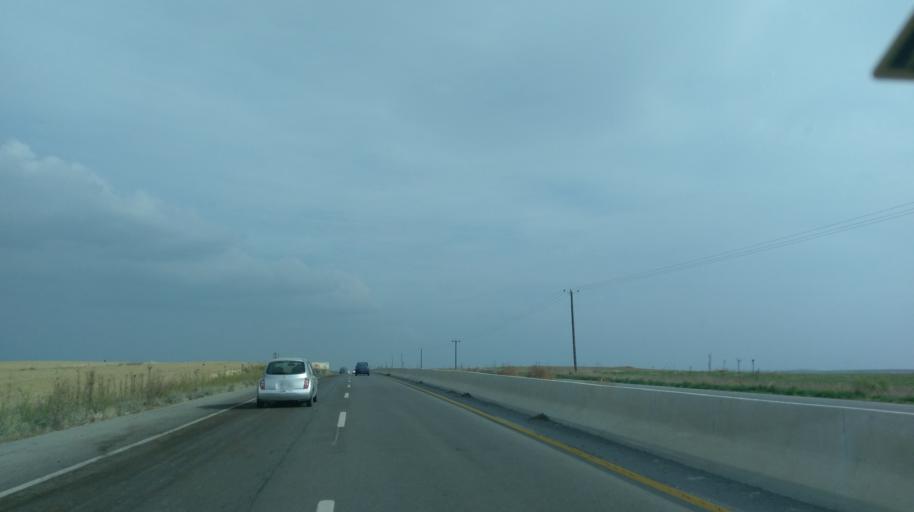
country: CY
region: Lefkosia
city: Mammari
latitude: 35.2125
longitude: 33.2029
